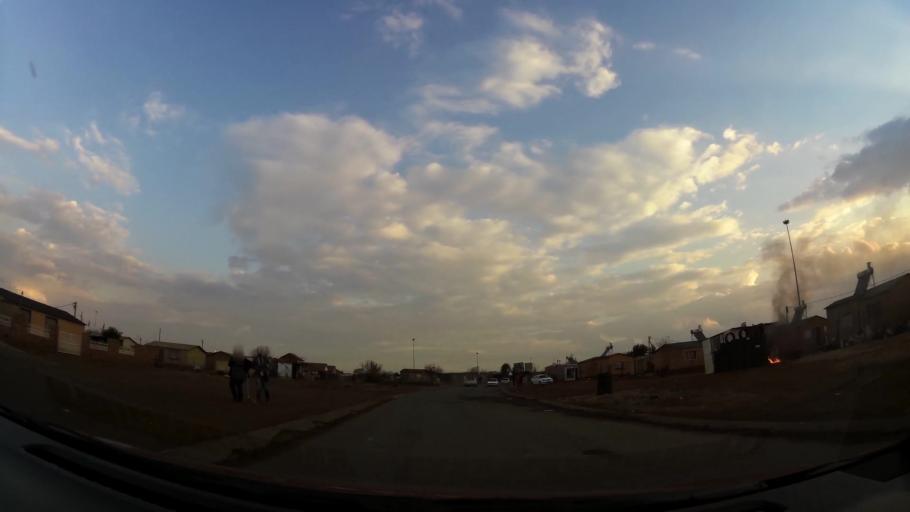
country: ZA
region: Gauteng
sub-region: City of Johannesburg Metropolitan Municipality
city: Orange Farm
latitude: -26.5611
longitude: 27.8379
